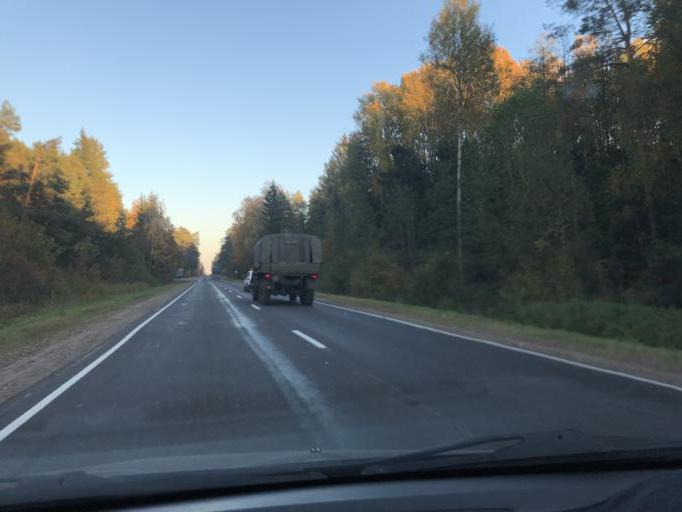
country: BY
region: Minsk
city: Staryya Darohi
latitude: 53.0413
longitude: 28.1639
